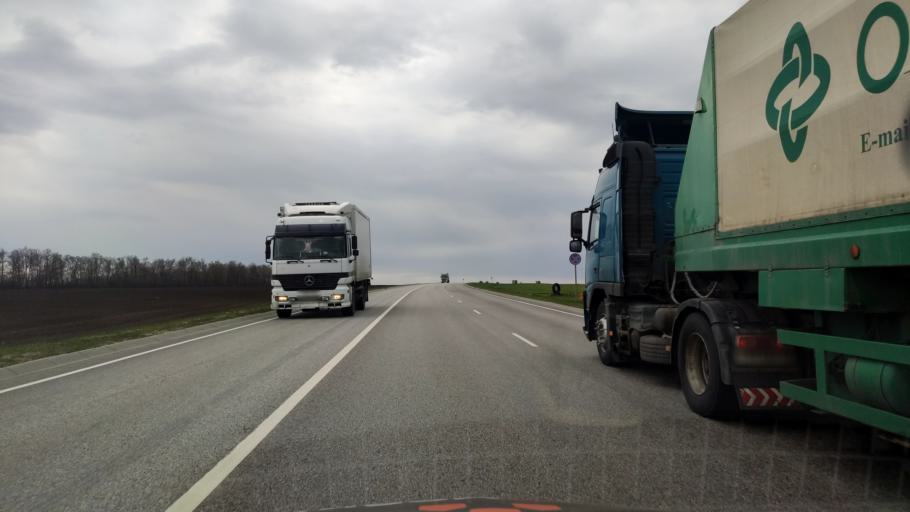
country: RU
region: Voronezj
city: Nizhnedevitsk
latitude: 51.5873
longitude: 38.5798
